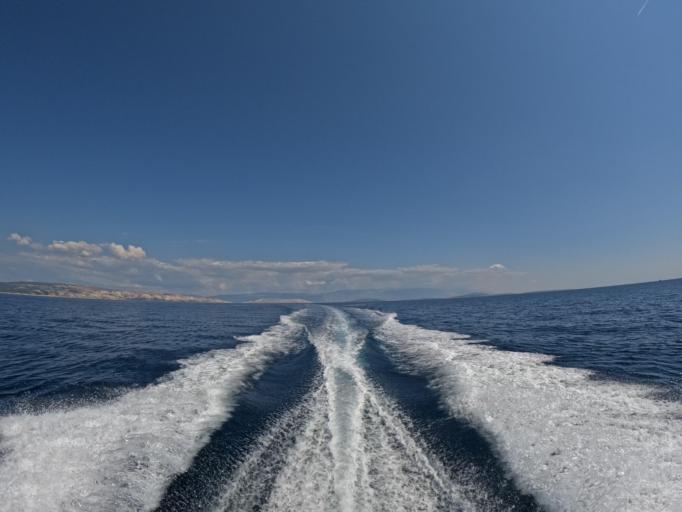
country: HR
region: Primorsko-Goranska
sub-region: Grad Krk
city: Krk
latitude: 44.9255
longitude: 14.5396
